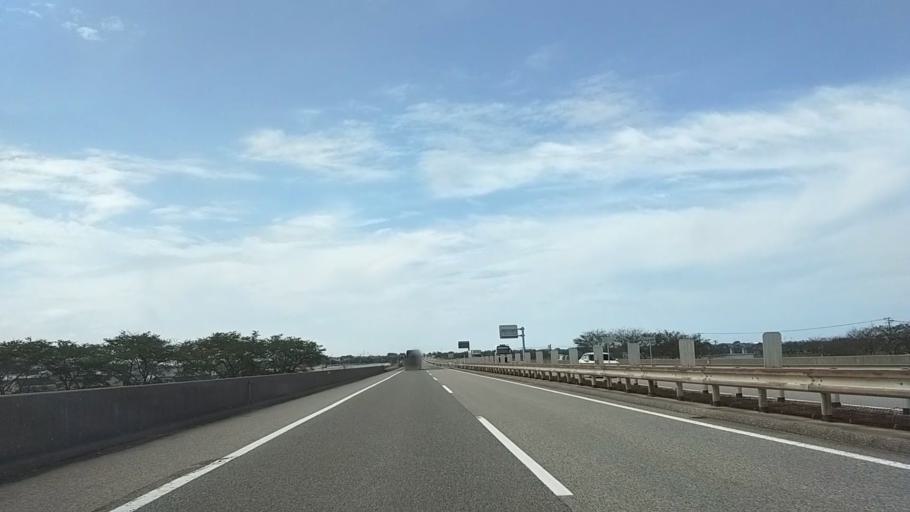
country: JP
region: Toyama
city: Nyuzen
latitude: 36.9388
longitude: 137.5481
